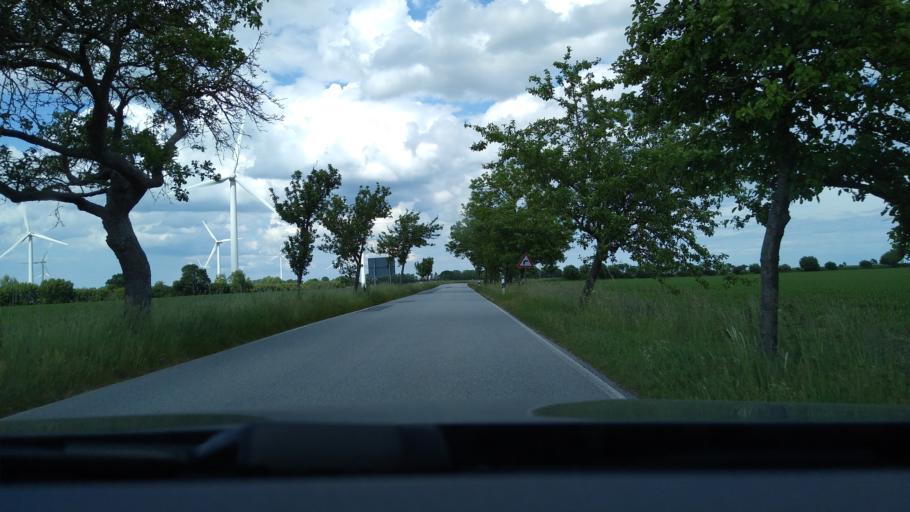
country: DE
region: Schleswig-Holstein
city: Riepsdorf
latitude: 54.2133
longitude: 10.9466
